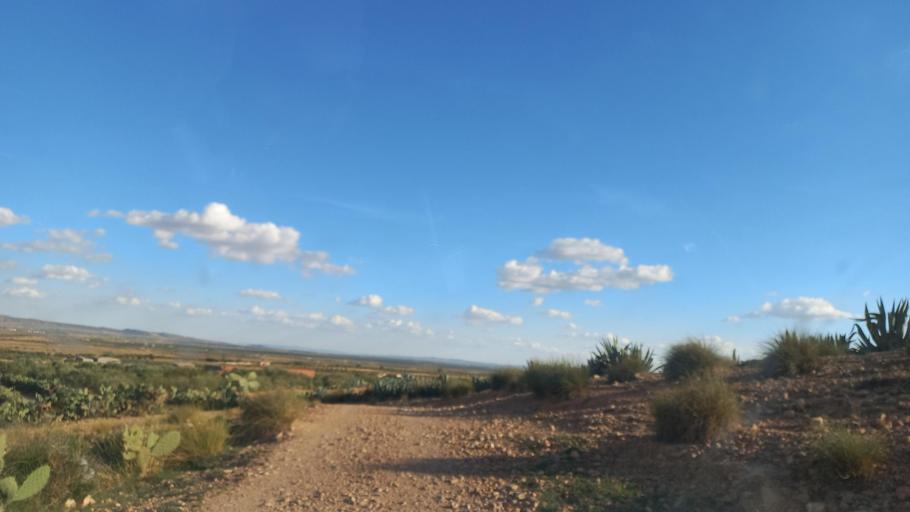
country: TN
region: Al Qasrayn
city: Sbiba
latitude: 35.3808
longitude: 9.0162
